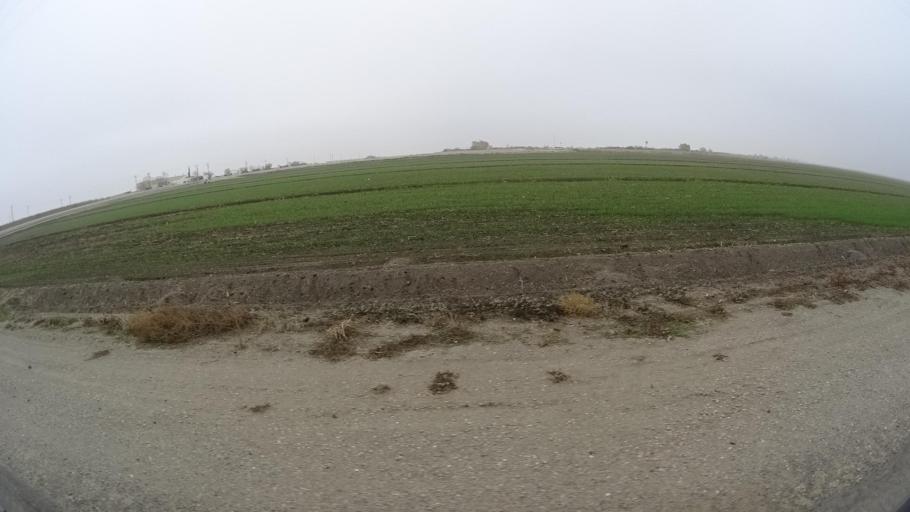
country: US
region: California
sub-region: Kern County
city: Rosedale
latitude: 35.2105
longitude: -119.2324
